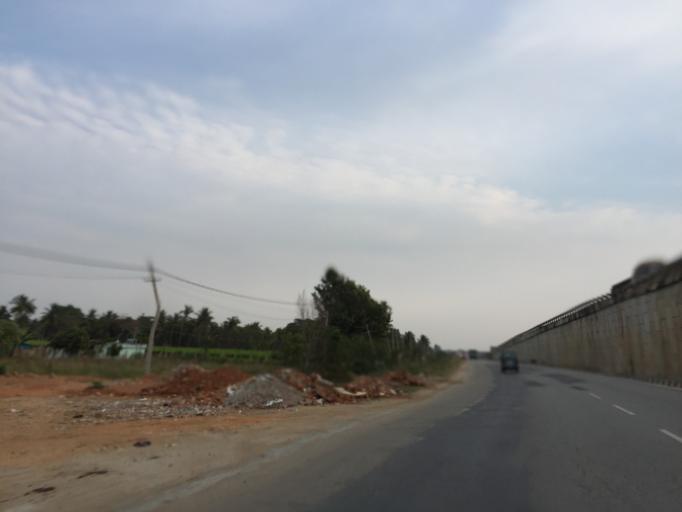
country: IN
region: Karnataka
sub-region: Chikkaballapur
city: Chik Ballapur
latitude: 13.4461
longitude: 77.7359
